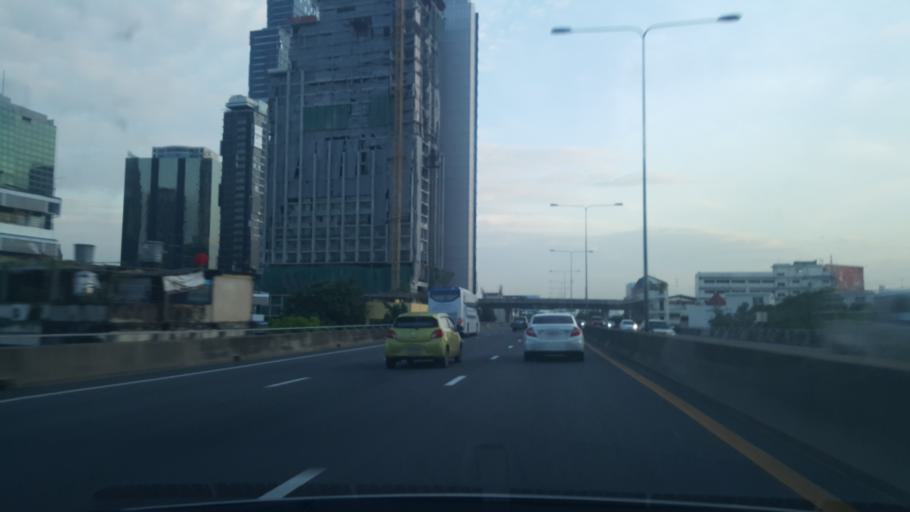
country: TH
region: Bangkok
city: Bang Rak
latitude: 13.7208
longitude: 100.5183
